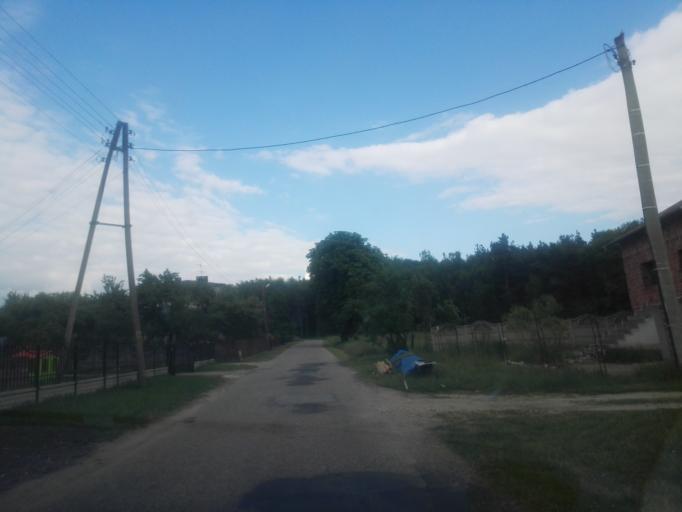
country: PL
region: Silesian Voivodeship
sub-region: Powiat czestochowski
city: Olsztyn
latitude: 50.7449
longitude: 19.3162
